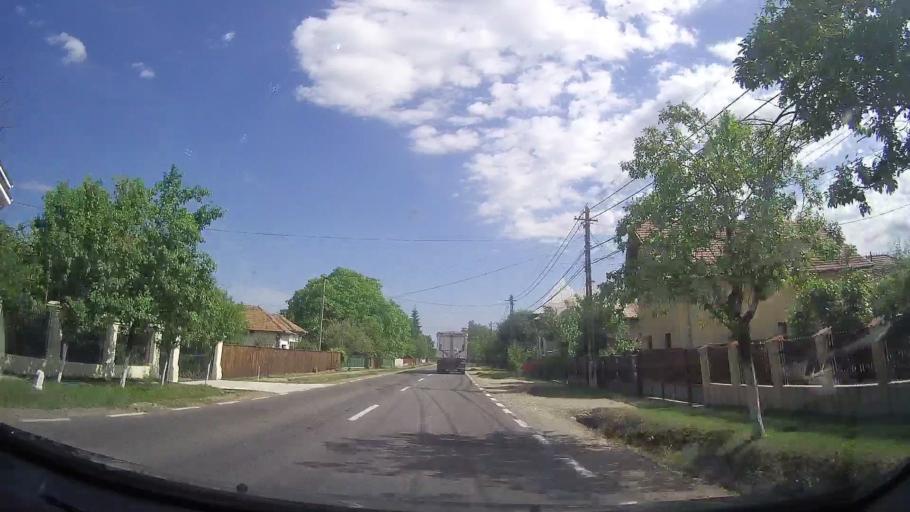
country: RO
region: Prahova
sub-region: Comuna Maneciu-Ungureni
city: Gheaba
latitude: 45.2996
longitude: 25.9986
